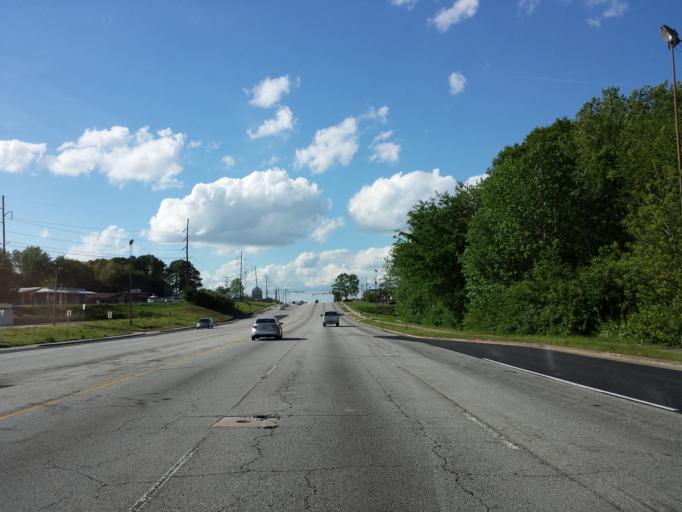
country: US
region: Georgia
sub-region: Cobb County
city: Fair Oaks
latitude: 33.8962
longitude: -84.5391
